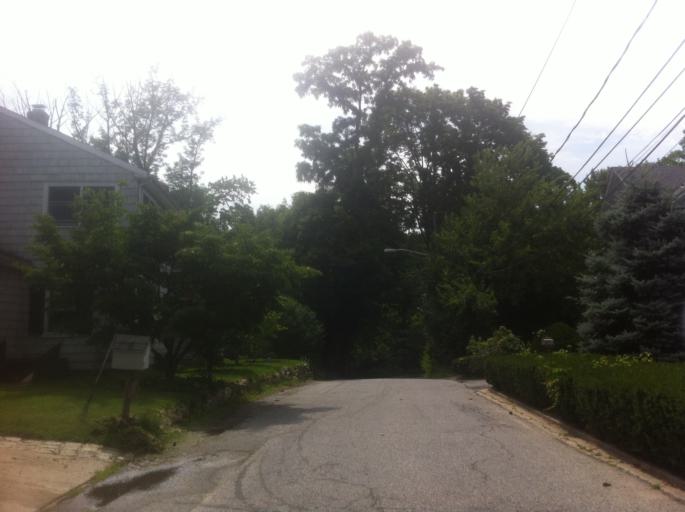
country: US
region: New York
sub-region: Nassau County
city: Locust Valley
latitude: 40.8817
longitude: -73.5851
